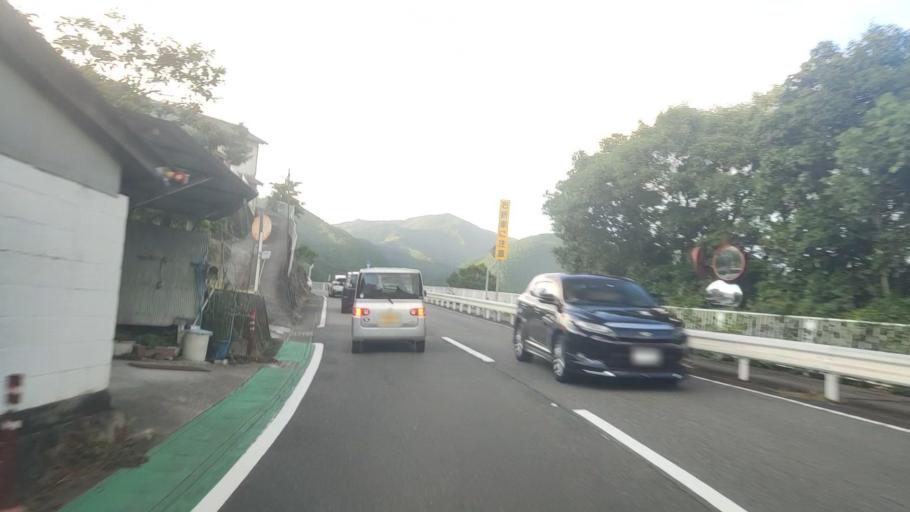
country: JP
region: Wakayama
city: Tanabe
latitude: 33.7212
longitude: 135.4814
